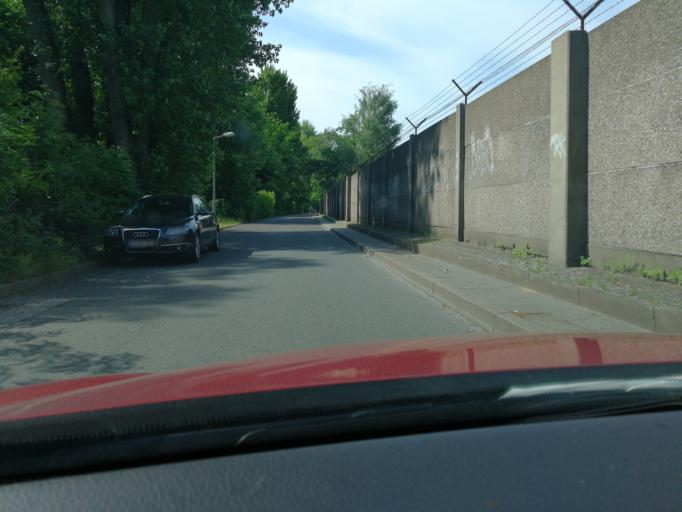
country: DE
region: Berlin
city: Reinickendorf
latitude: 52.5574
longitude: 13.3255
